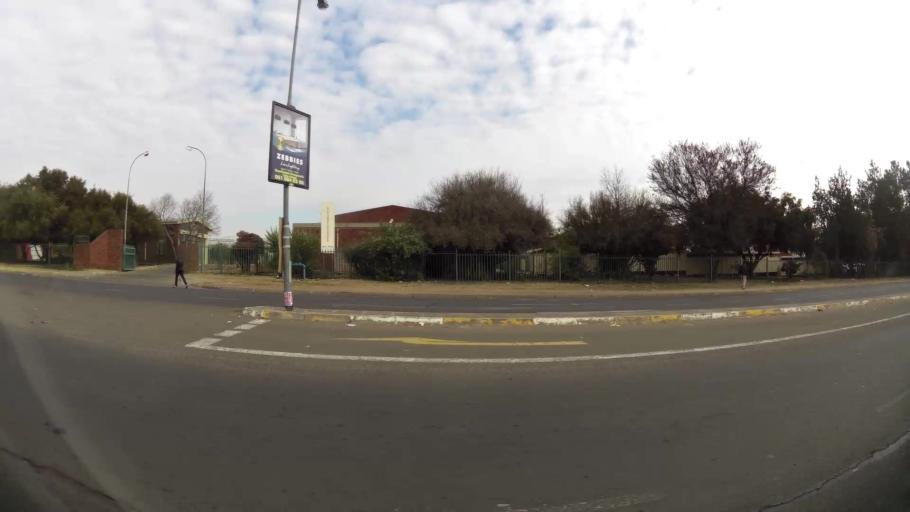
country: ZA
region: Orange Free State
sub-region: Mangaung Metropolitan Municipality
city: Bloemfontein
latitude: -29.1250
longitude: 26.2113
